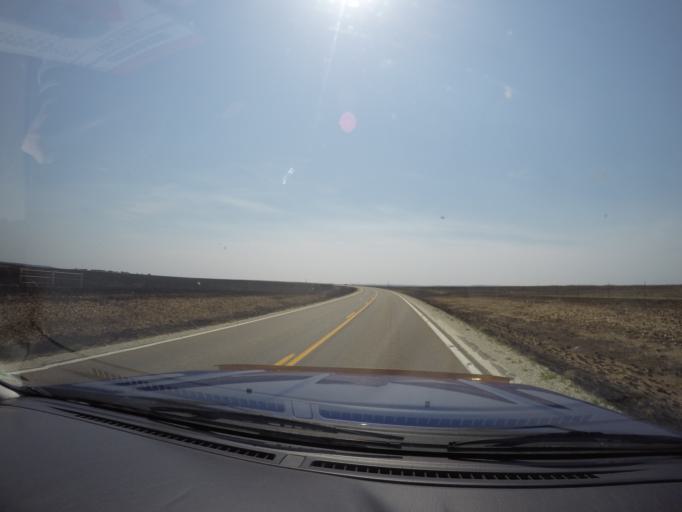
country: US
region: Kansas
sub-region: Chase County
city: Cottonwood Falls
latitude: 38.4996
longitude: -96.5554
